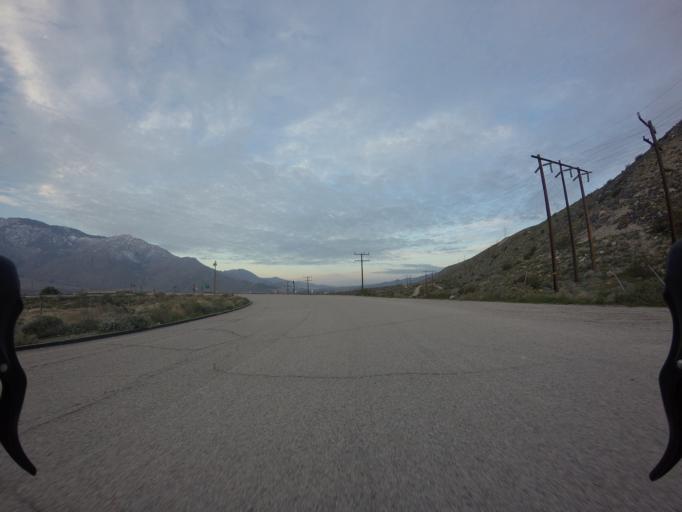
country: US
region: California
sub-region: Riverside County
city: Garnet
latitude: 33.9248
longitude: -116.6433
